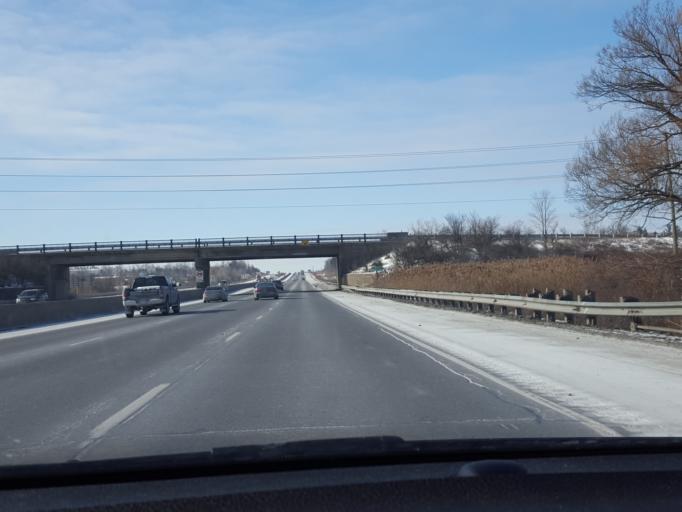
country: CA
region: Ontario
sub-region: Halton
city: Milton
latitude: 43.5223
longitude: -79.9335
